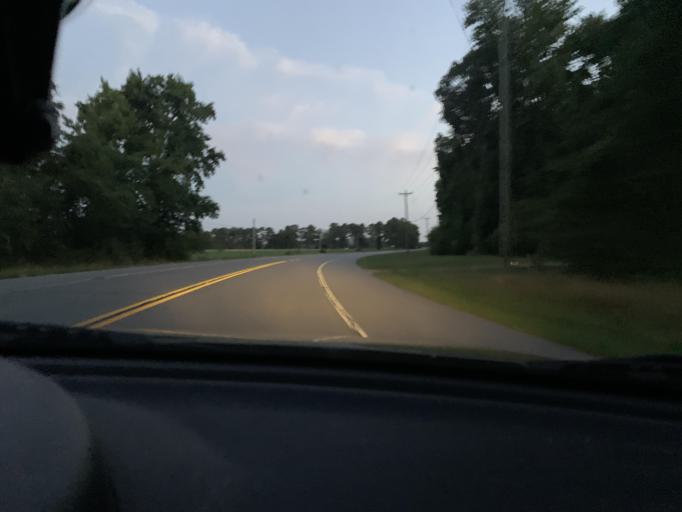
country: US
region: Maryland
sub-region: Talbot County
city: Saint Michaels
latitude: 38.7572
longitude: -76.3193
